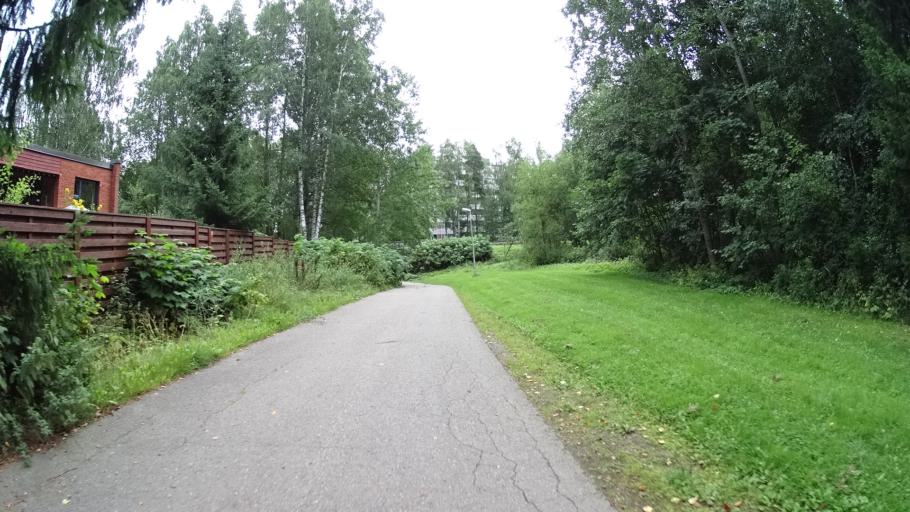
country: FI
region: Uusimaa
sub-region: Helsinki
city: Teekkarikylae
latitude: 60.2740
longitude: 24.8531
